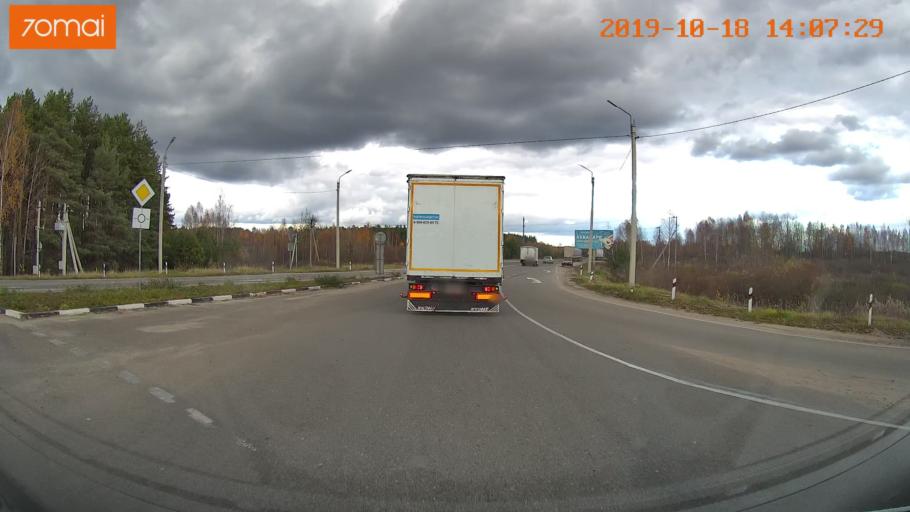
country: RU
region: Rjazan
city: Spas-Klepiki
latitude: 55.1510
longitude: 40.1596
